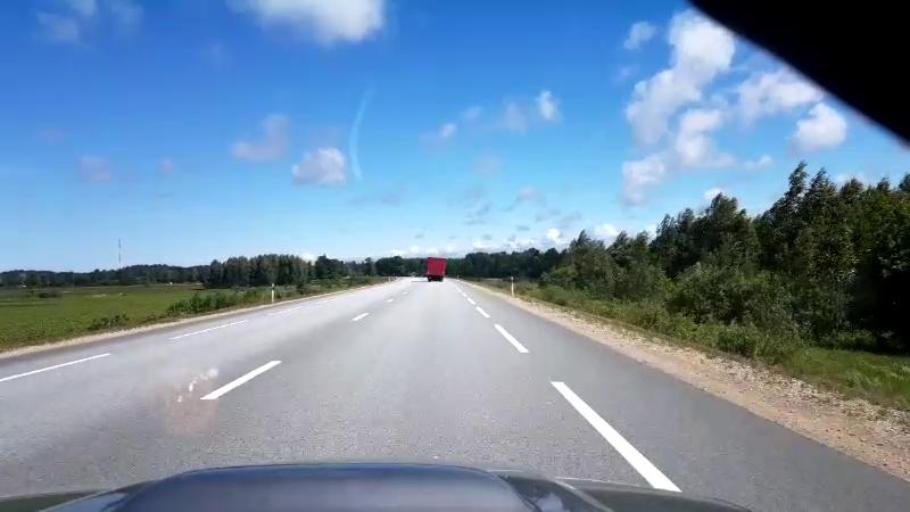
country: LV
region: Adazi
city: Adazi
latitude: 57.1112
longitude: 24.3206
